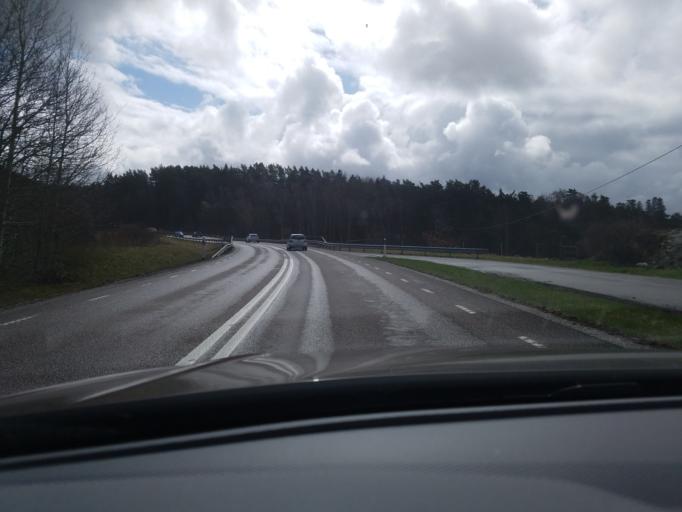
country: SE
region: Vaestra Goetaland
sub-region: Tjorns Kommun
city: Myggenas
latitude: 58.0680
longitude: 11.6993
